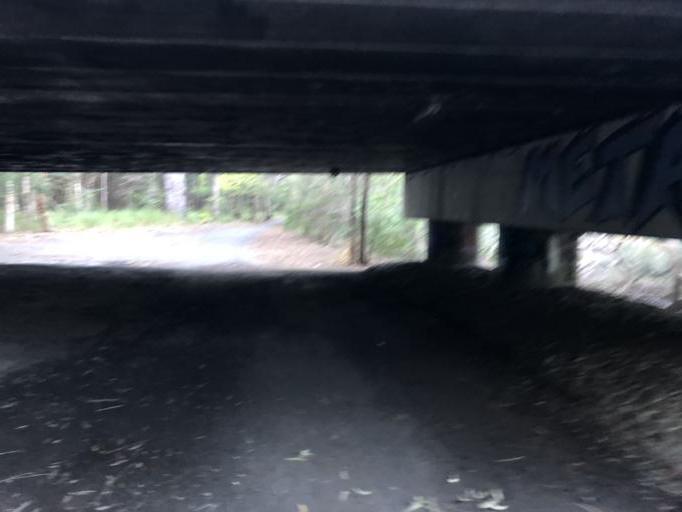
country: AU
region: New South Wales
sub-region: Coffs Harbour
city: Coffs Harbour
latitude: -30.3003
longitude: 153.1259
